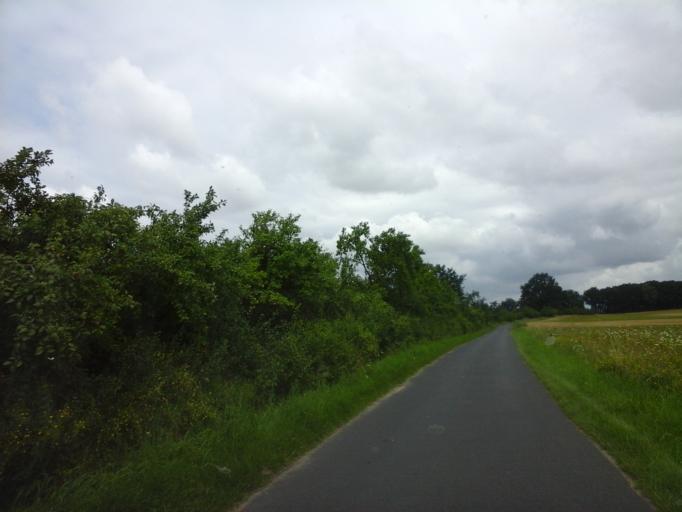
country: PL
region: West Pomeranian Voivodeship
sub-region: Powiat choszczenski
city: Pelczyce
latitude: 52.9936
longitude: 15.3689
